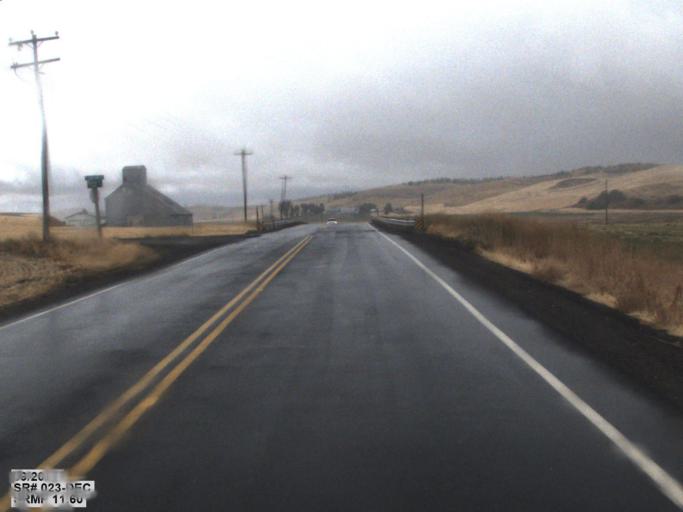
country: US
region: Washington
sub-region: Whitman County
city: Colfax
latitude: 47.0754
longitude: -117.5368
